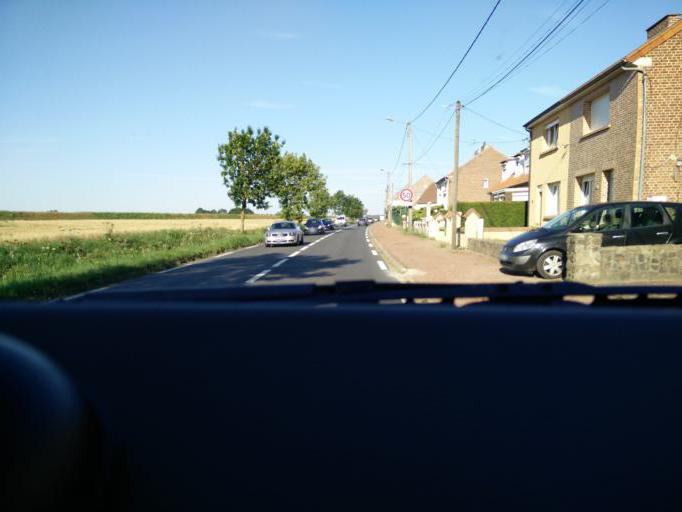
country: FR
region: Nord-Pas-de-Calais
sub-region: Departement du Pas-de-Calais
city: Houdain
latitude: 50.4524
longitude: 2.5538
